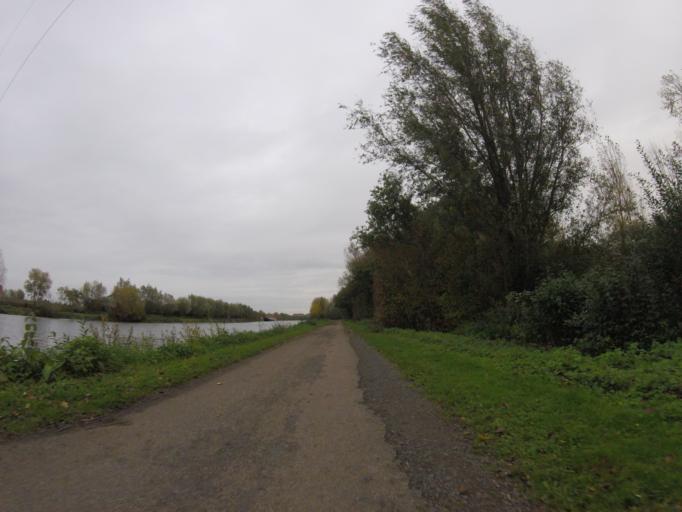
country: FR
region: Nord-Pas-de-Calais
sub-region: Departement du Nord
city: Wambrechies
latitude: 50.6928
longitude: 3.0388
